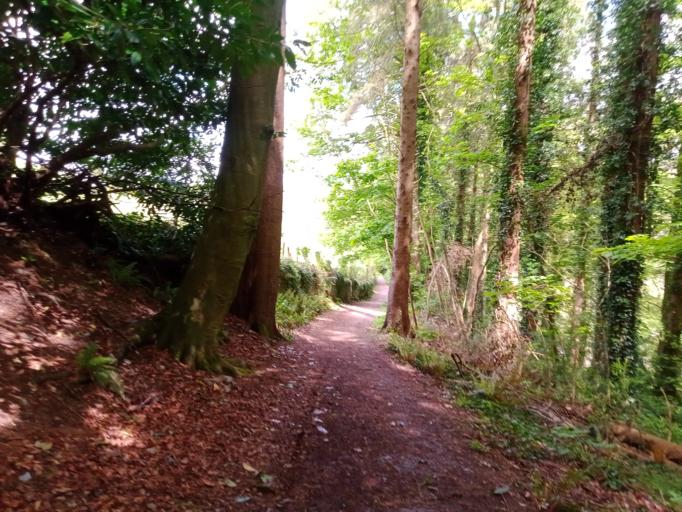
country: IE
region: Leinster
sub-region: Kilkenny
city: Thomastown
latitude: 52.4847
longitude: -7.0670
